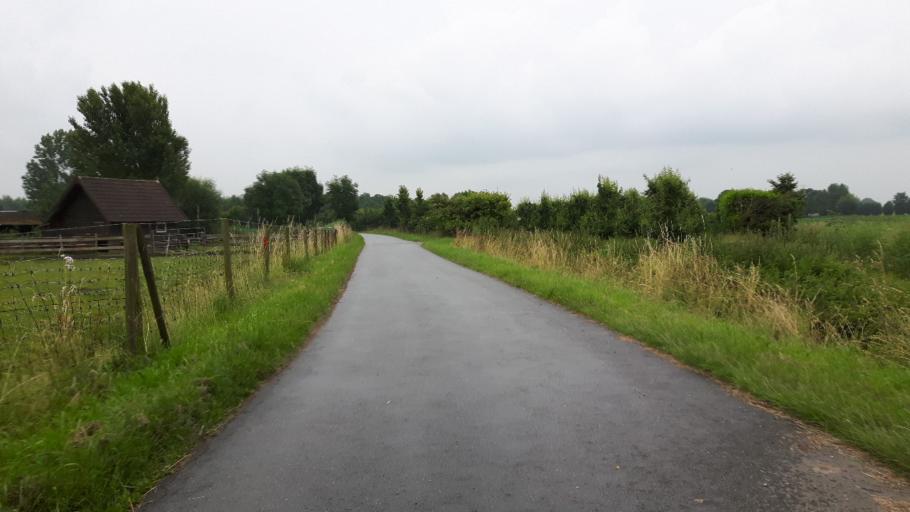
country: NL
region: Utrecht
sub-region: Gemeente Lopik
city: Lopik
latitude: 51.9682
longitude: 4.9683
